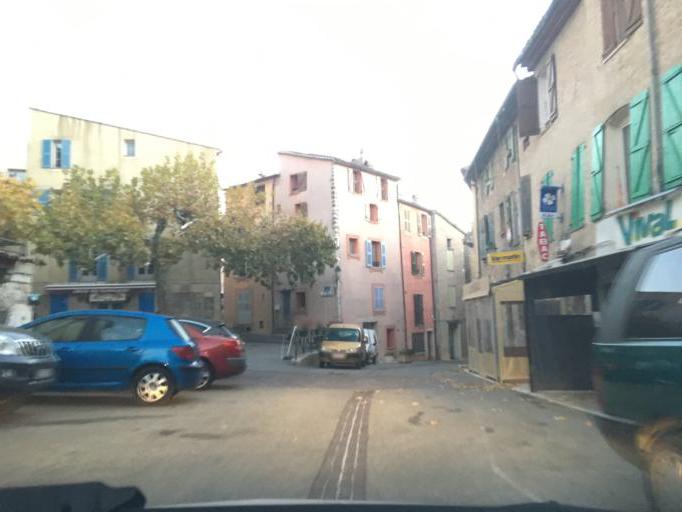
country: FR
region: Provence-Alpes-Cote d'Azur
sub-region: Departement du Var
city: Montferrat
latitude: 43.6133
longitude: 6.4815
